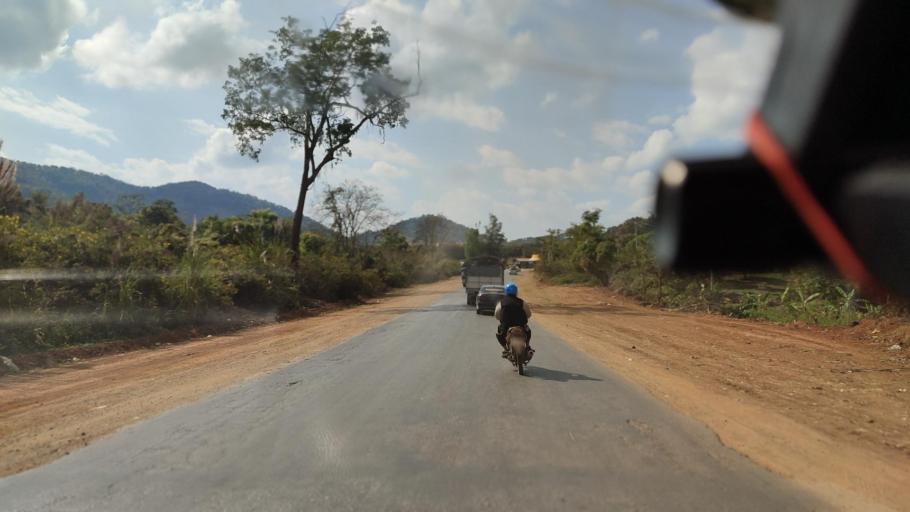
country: MM
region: Shan
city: Lashio
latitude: 23.0934
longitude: 97.8128
